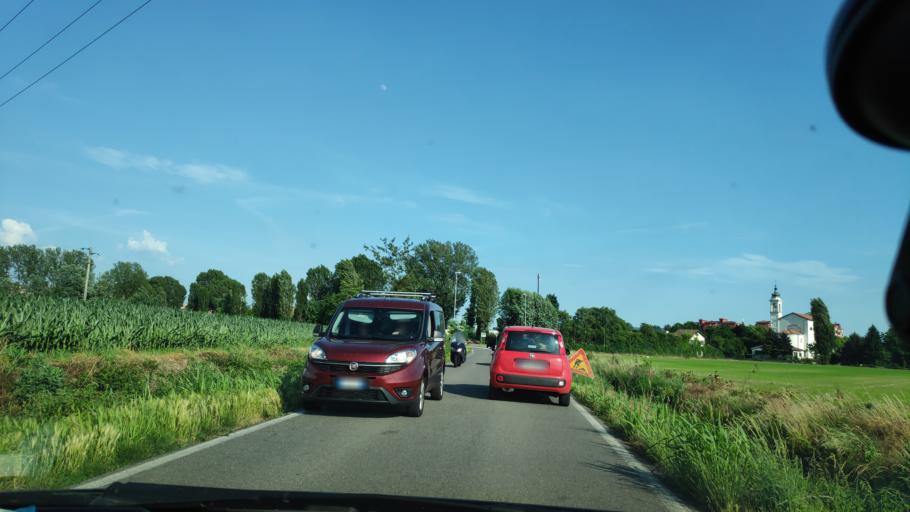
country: IT
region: Lombardy
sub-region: Citta metropolitana di Milano
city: Opera
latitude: 45.3834
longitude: 9.2060
